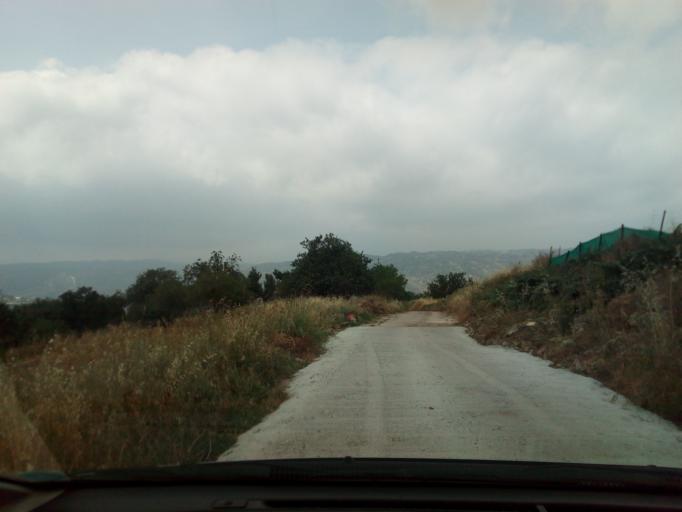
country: CY
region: Limassol
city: Pachna
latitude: 34.8127
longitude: 32.6475
